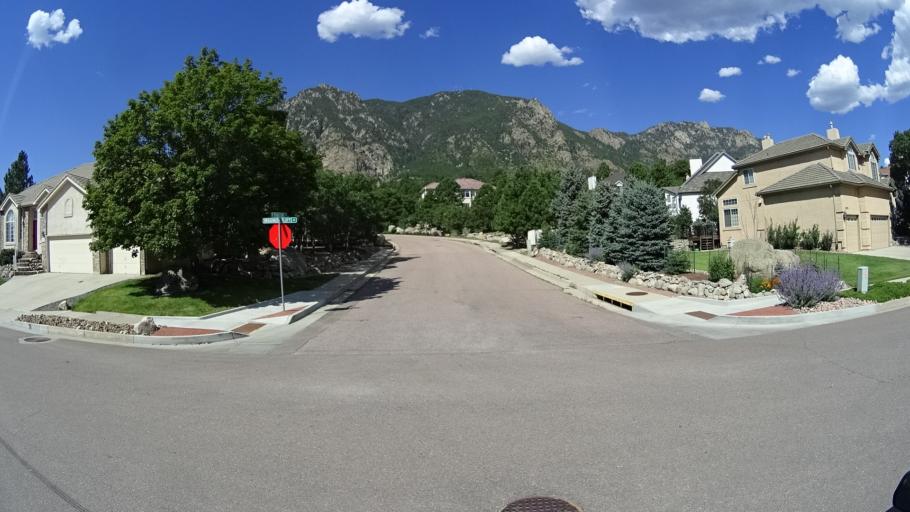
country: US
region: Colorado
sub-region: El Paso County
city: Fort Carson
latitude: 38.7479
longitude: -104.8337
